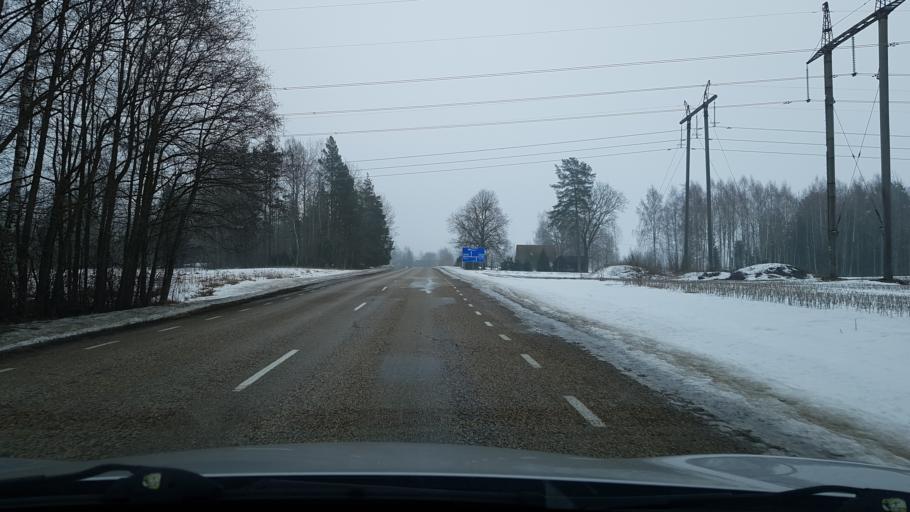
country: EE
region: Valgamaa
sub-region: Torva linn
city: Torva
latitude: 58.0554
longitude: 26.1858
